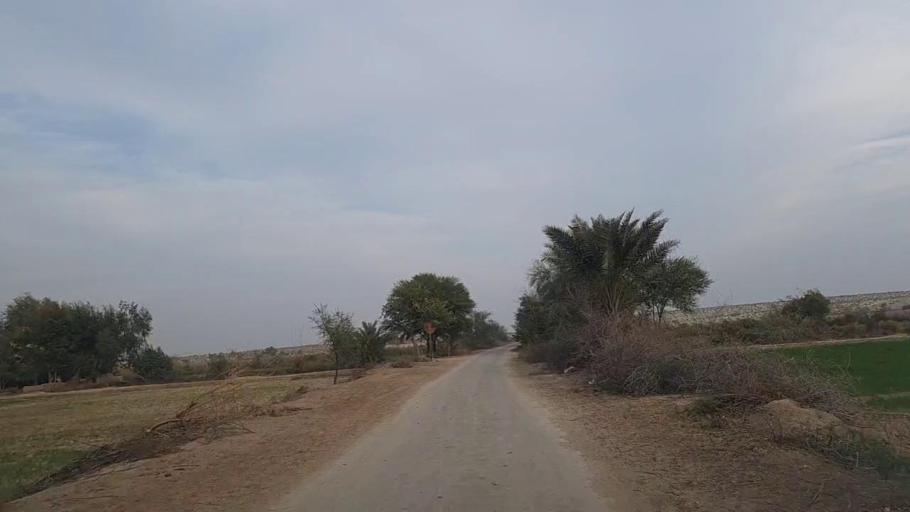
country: PK
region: Sindh
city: Daur
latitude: 26.5156
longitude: 68.4865
